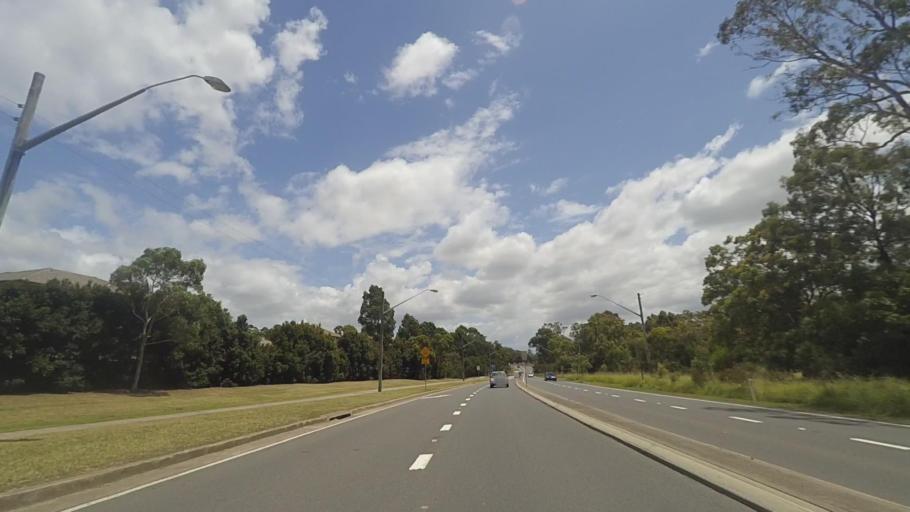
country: AU
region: New South Wales
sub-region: Liverpool
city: Holsworthy
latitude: -33.9603
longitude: 150.9589
